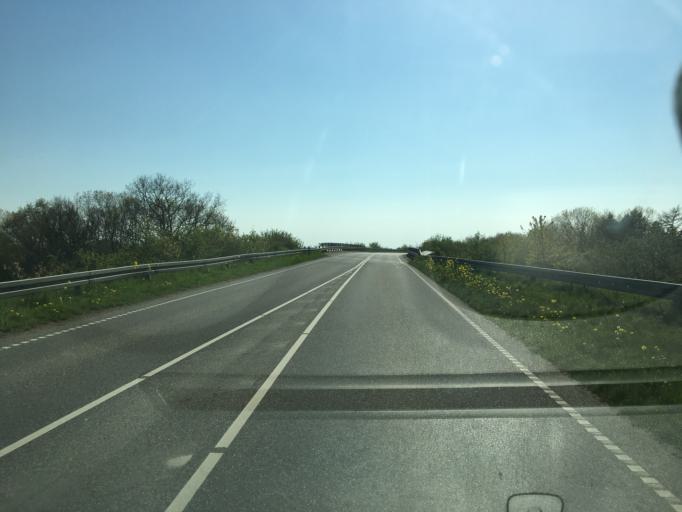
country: DK
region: South Denmark
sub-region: Haderslev Kommune
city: Vojens
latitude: 55.3115
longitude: 9.2892
